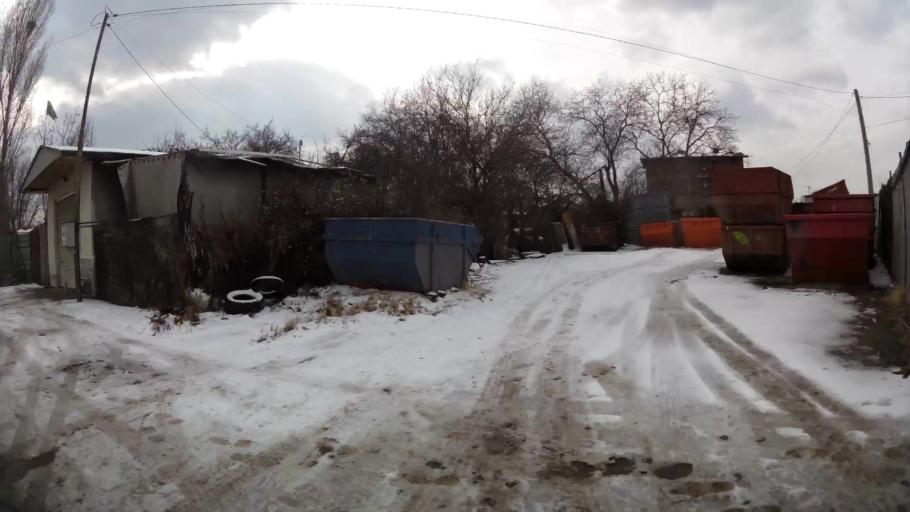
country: BG
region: Sofia-Capital
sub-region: Stolichna Obshtina
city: Sofia
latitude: 42.7084
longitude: 23.3753
